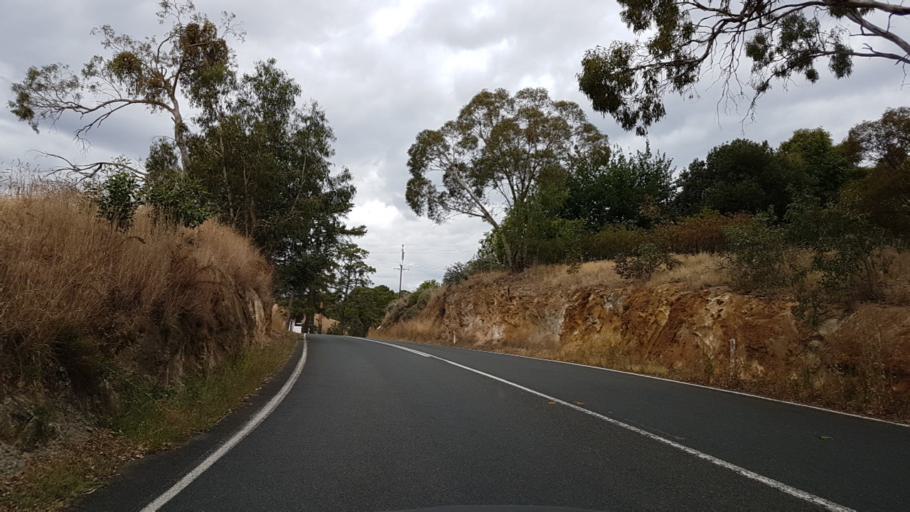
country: AU
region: South Australia
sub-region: Adelaide Hills
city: Gumeracha
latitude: -34.7746
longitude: 138.8759
